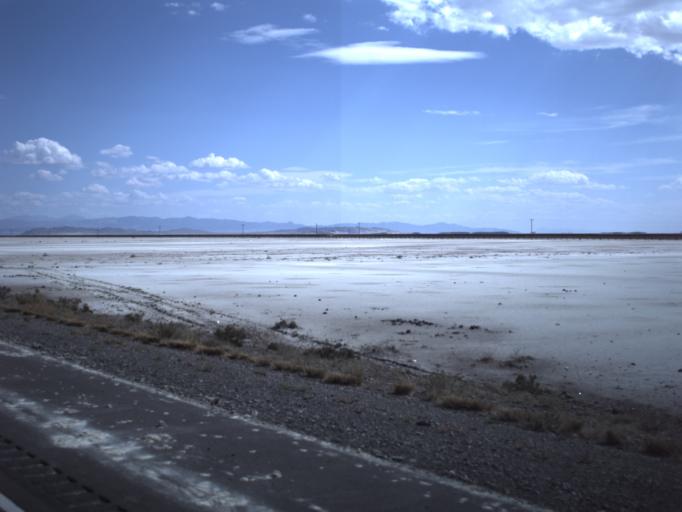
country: US
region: Utah
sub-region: Tooele County
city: Wendover
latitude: 40.7302
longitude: -113.4694
